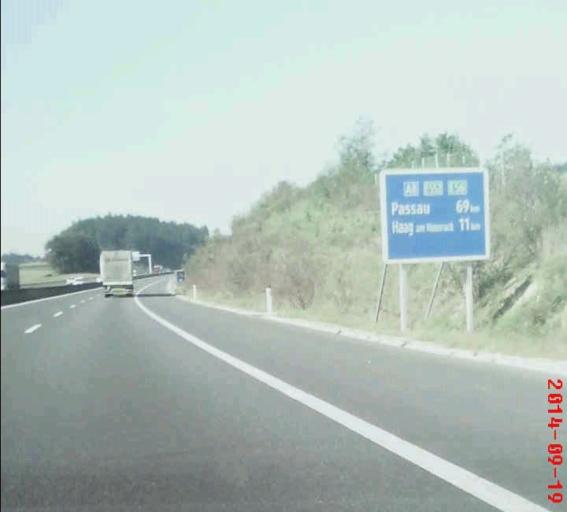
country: AT
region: Upper Austria
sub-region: Wels-Land
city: Offenhausen
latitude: 48.1795
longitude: 13.7781
